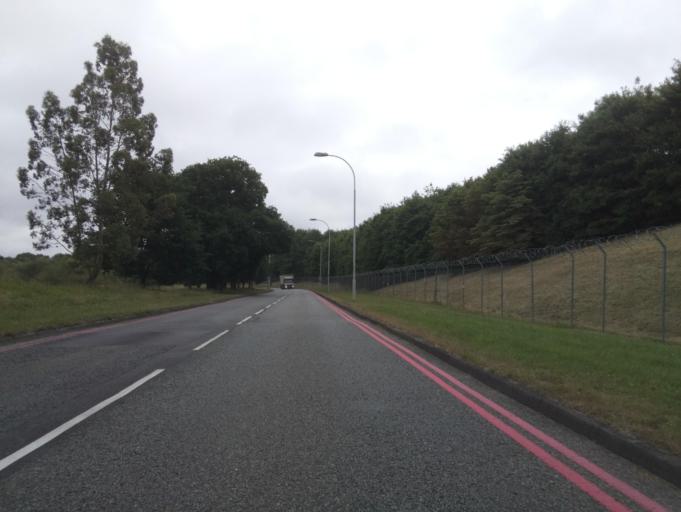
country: GB
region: England
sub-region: Surrey
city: Horley
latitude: 51.1615
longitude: -0.1872
